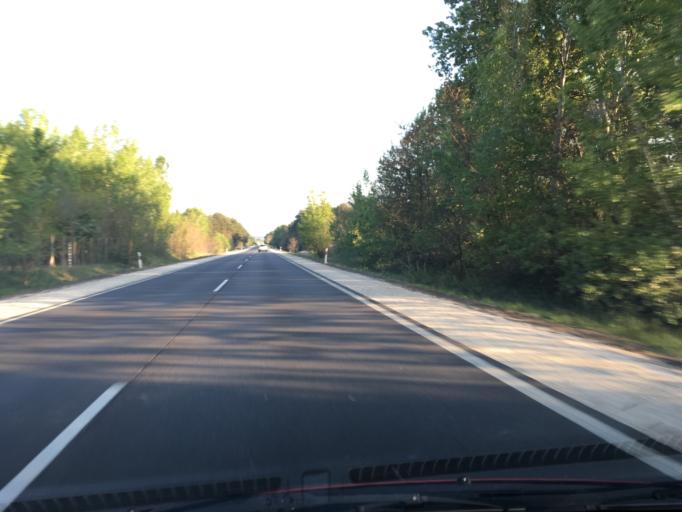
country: HU
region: Pest
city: Szod
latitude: 47.7121
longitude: 19.1621
